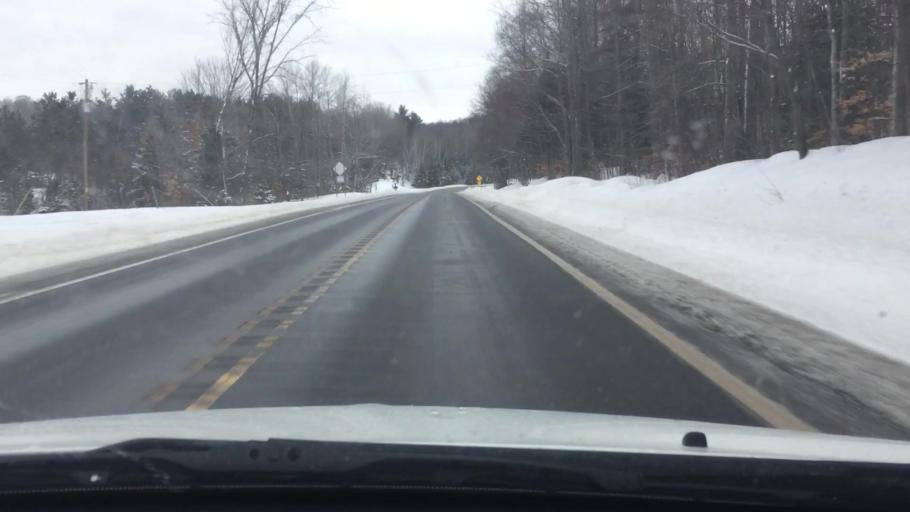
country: US
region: Michigan
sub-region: Charlevoix County
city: East Jordan
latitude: 45.1127
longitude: -85.0603
